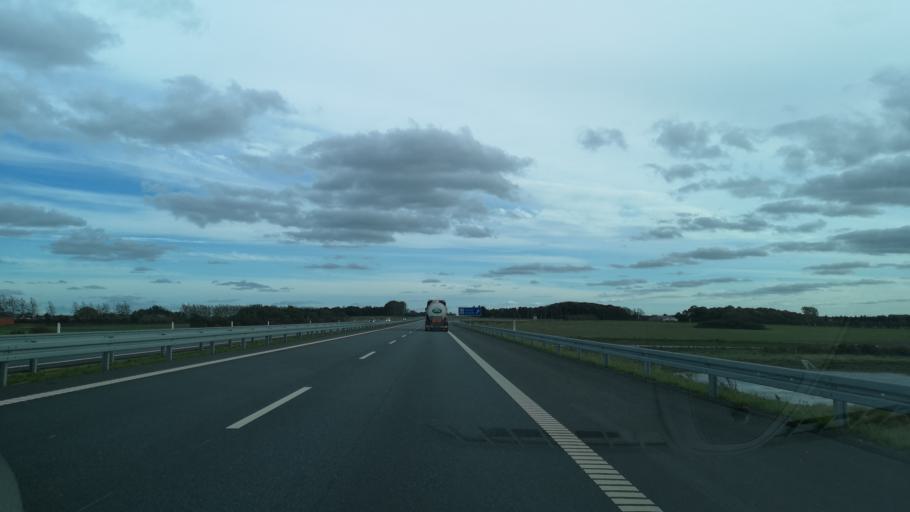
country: DK
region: Central Jutland
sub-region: Herning Kommune
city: Avlum
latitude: 56.2593
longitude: 8.7734
